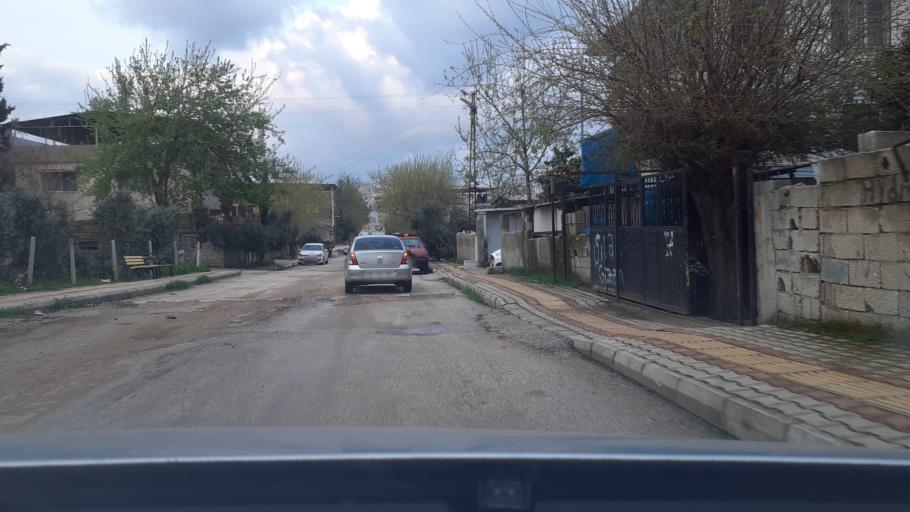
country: TR
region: Hatay
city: Kirikhan
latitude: 36.4834
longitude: 36.3485
